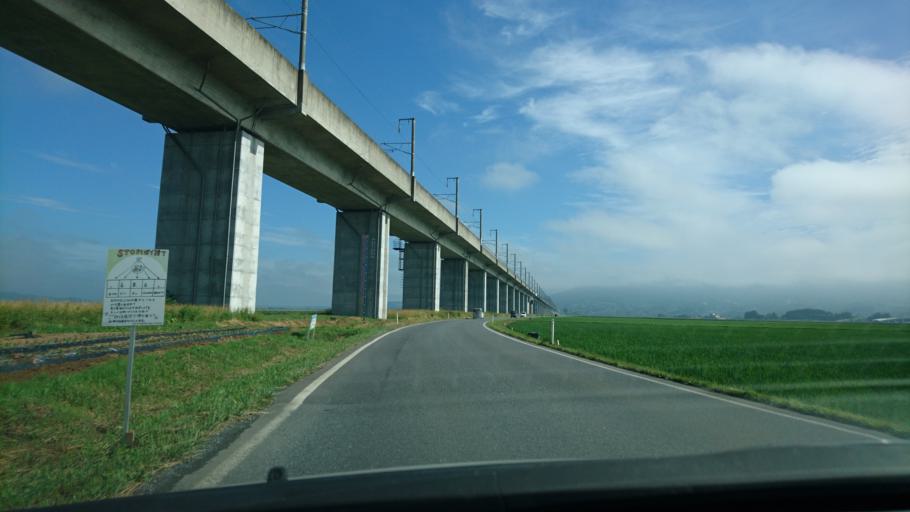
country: JP
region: Iwate
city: Ichinoseki
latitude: 38.9439
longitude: 141.1467
